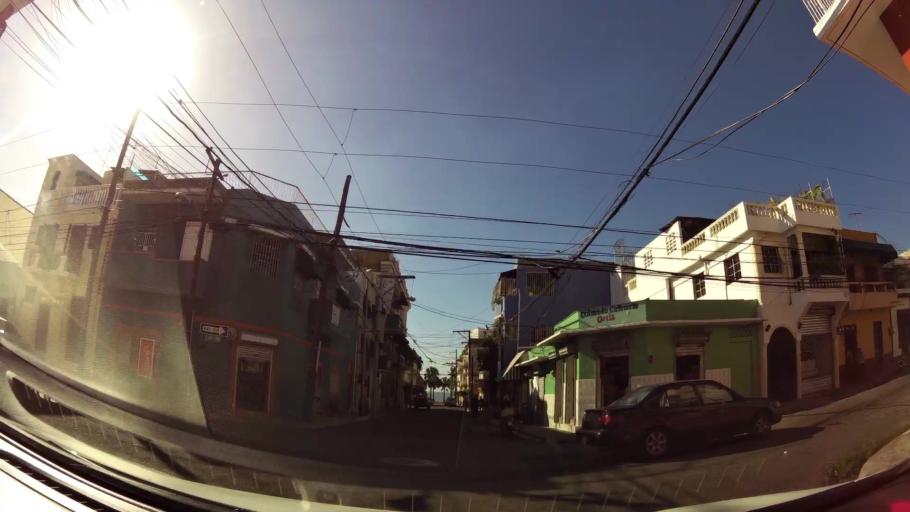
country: DO
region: Nacional
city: Ciudad Nueva
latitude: 18.4679
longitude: -69.8917
